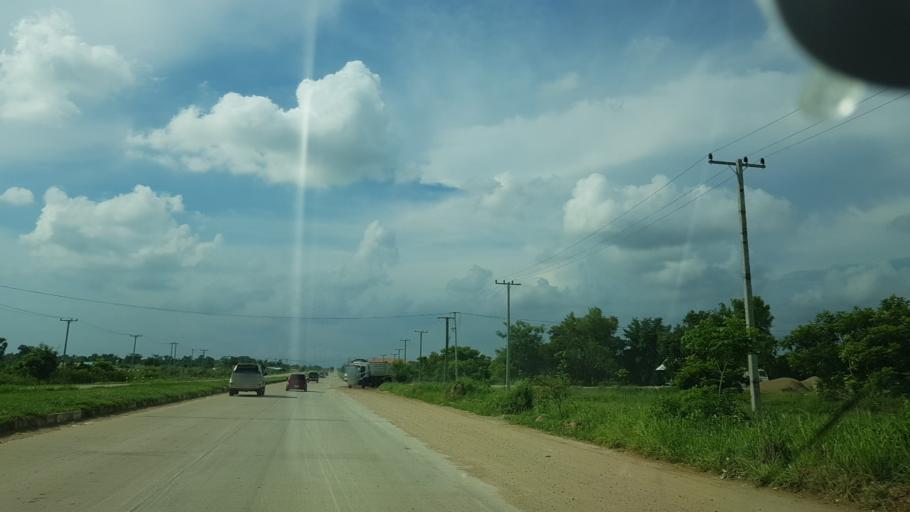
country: TH
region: Nong Khai
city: Nong Khai
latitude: 17.9280
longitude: 102.7194
